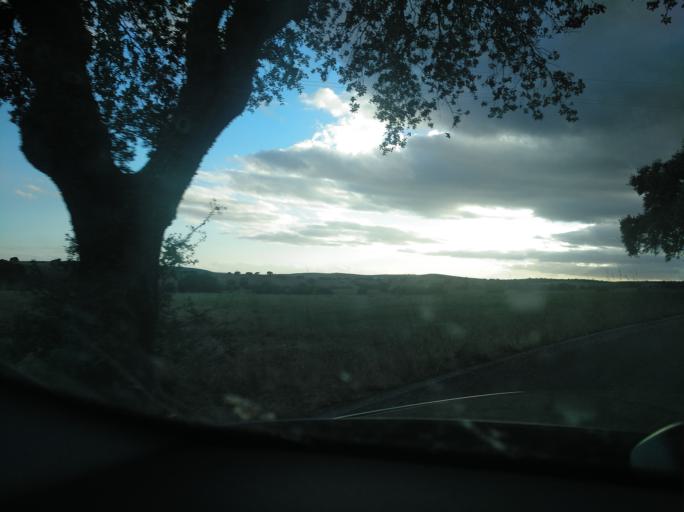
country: PT
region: Portalegre
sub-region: Campo Maior
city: Campo Maior
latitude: 39.0455
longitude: -7.0042
